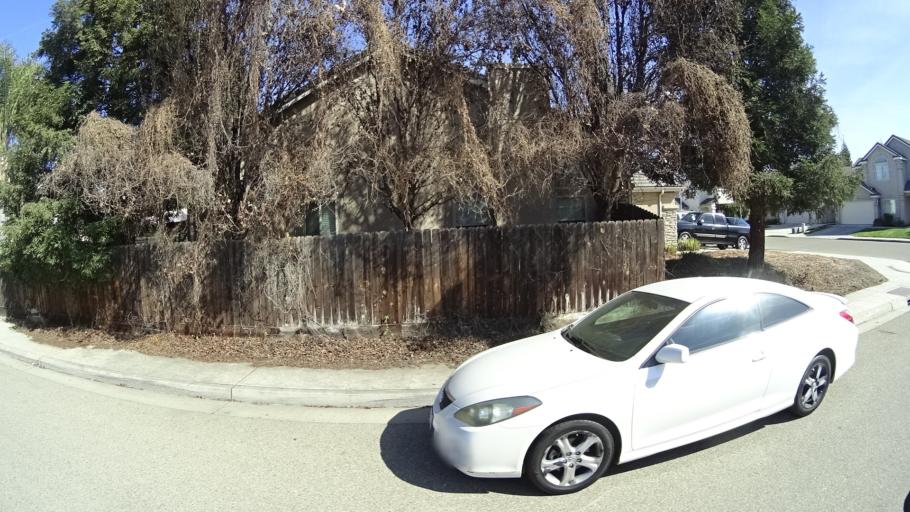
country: US
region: California
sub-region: Fresno County
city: Clovis
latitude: 36.8473
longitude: -119.7339
